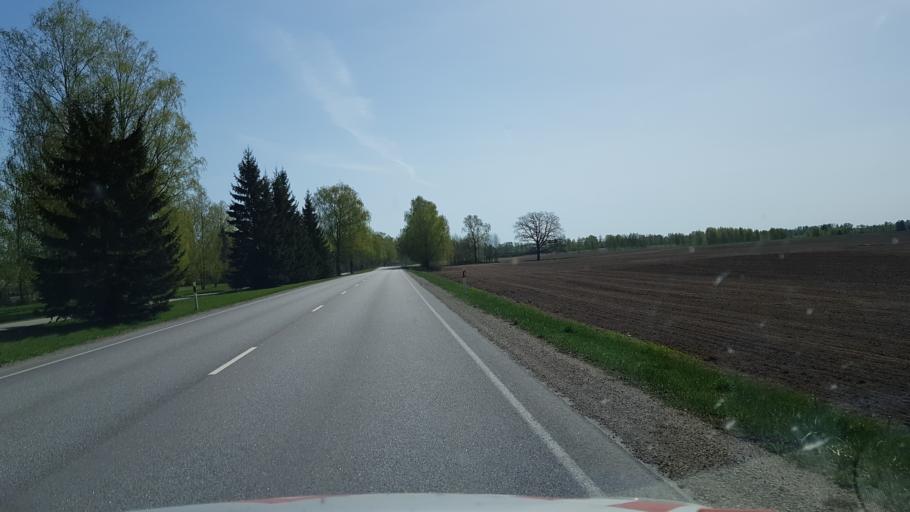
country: EE
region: Valgamaa
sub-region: Torva linn
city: Torva
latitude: 58.0301
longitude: 25.8511
